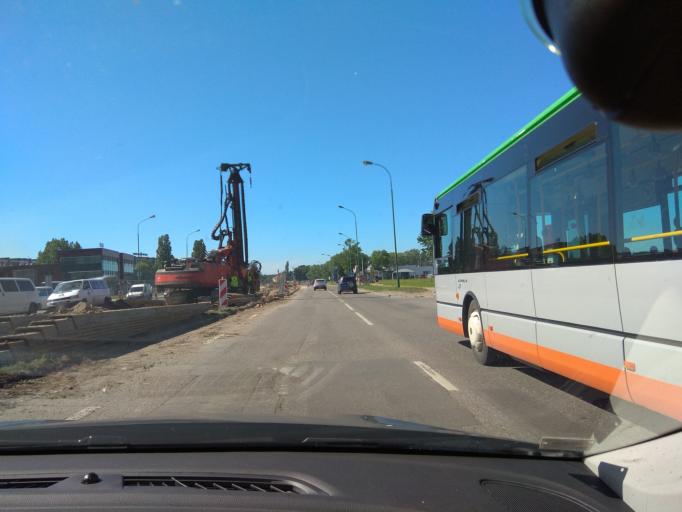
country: LT
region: Klaipedos apskritis
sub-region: Klaipeda
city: Klaipeda
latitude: 55.7010
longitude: 21.1667
